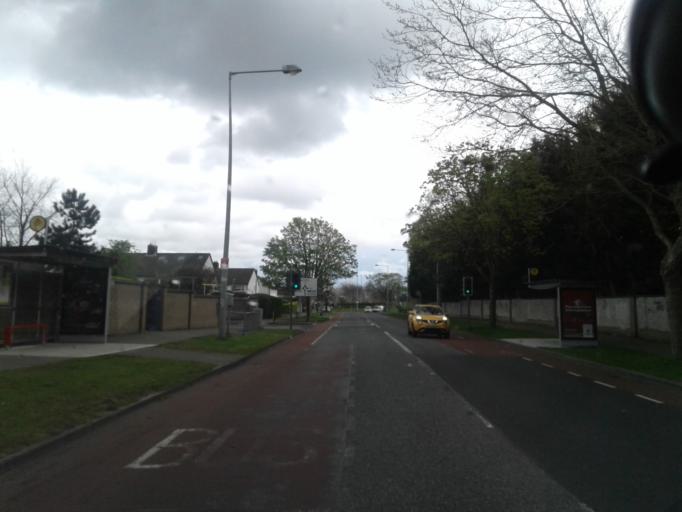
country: IE
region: Leinster
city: Templeogue
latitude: 53.3035
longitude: -6.3117
